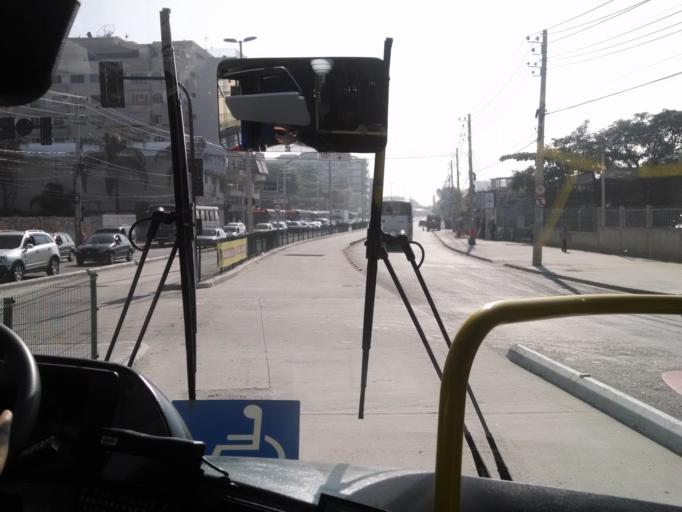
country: BR
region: Rio de Janeiro
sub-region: Sao Joao De Meriti
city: Sao Joao de Meriti
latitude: -22.8925
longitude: -43.3483
